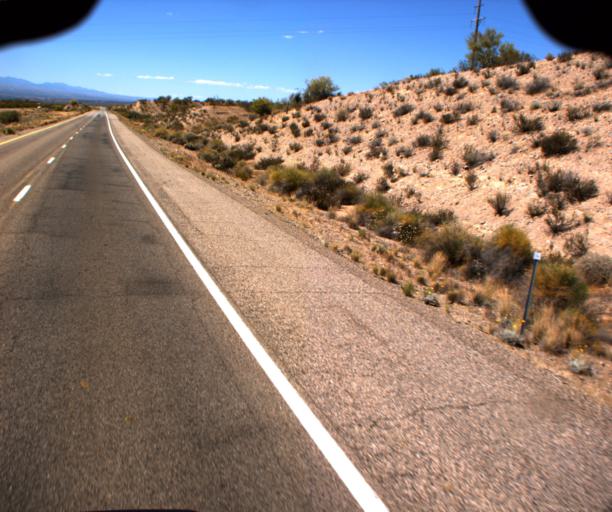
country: US
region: Arizona
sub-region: Yavapai County
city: Bagdad
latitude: 34.5971
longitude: -113.5169
